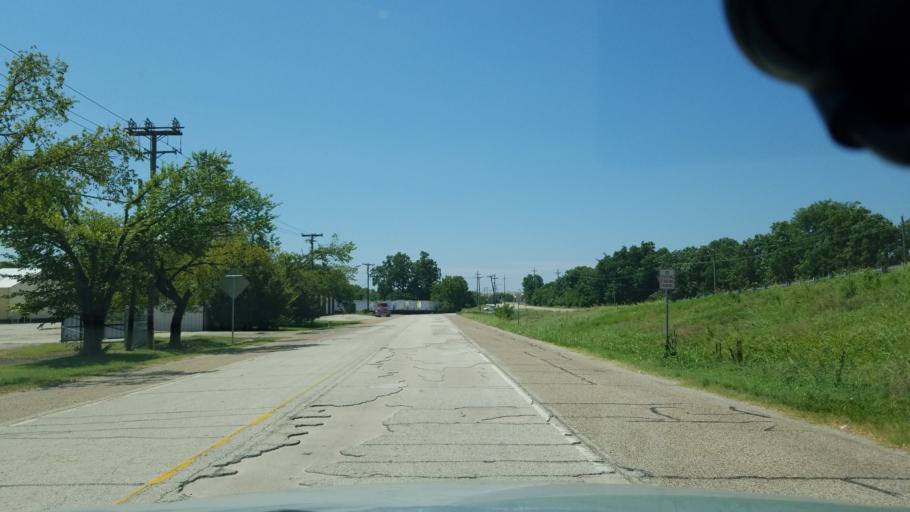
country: US
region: Texas
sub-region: Tarrant County
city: Euless
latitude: 32.8360
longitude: -97.0299
